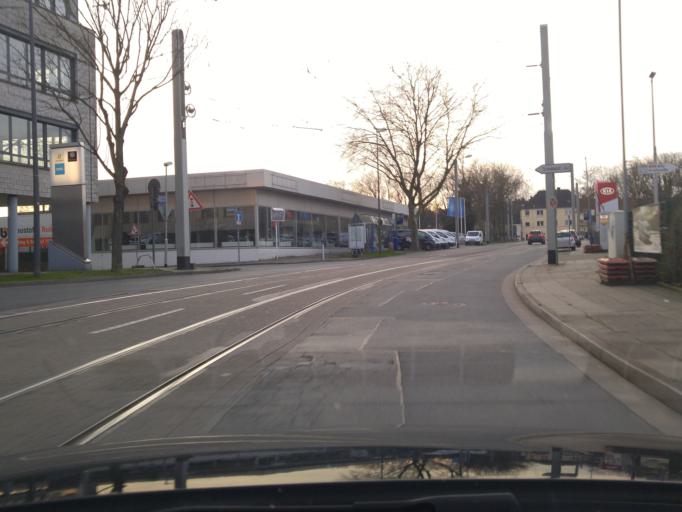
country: DE
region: North Rhine-Westphalia
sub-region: Regierungsbezirk Dusseldorf
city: Essen
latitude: 51.4286
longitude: 7.0416
